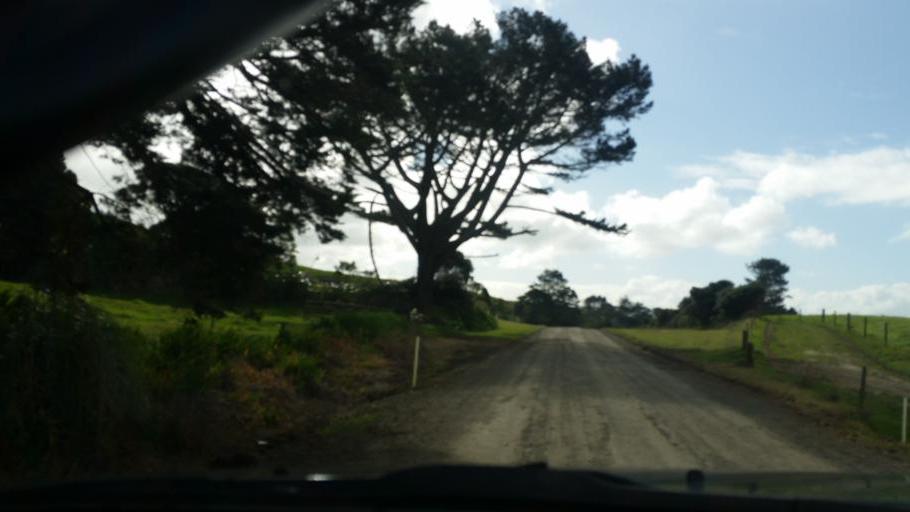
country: NZ
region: Northland
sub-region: Kaipara District
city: Dargaville
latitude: -36.0665
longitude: 173.8784
